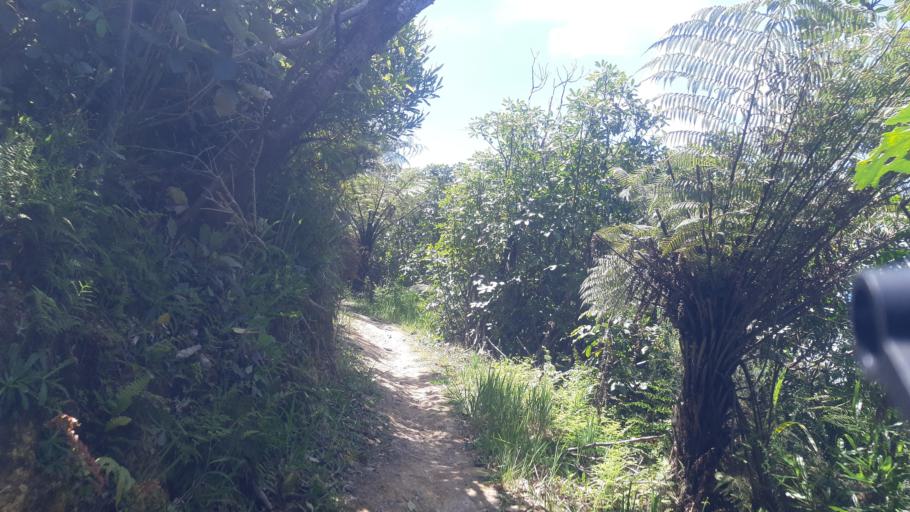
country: NZ
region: Marlborough
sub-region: Marlborough District
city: Picton
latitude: -41.2670
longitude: 174.0302
